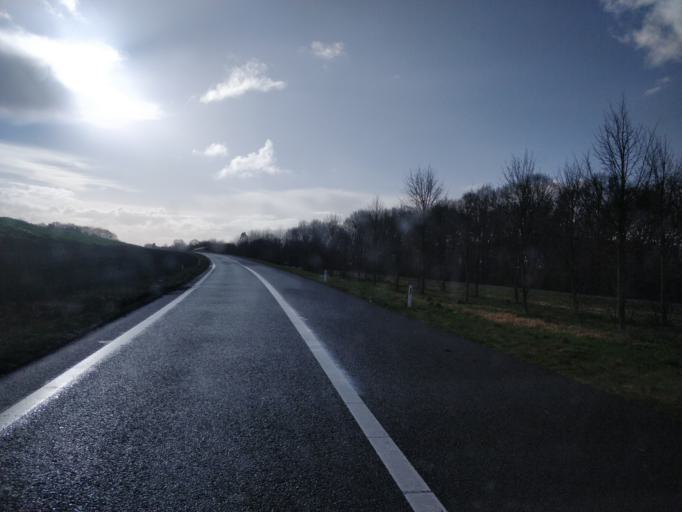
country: NL
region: Friesland
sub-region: Gemeente Heerenveen
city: Oranjewoud
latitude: 52.9520
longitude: 5.9412
